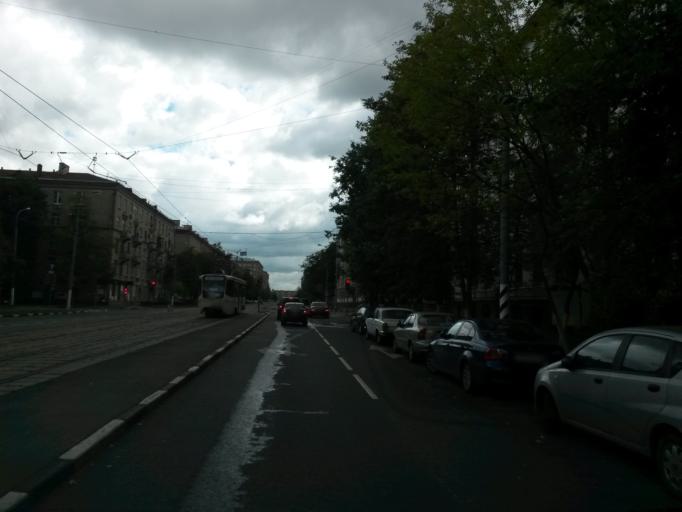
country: RU
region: Moskovskaya
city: Semenovskoye
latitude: 55.6840
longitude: 37.5586
